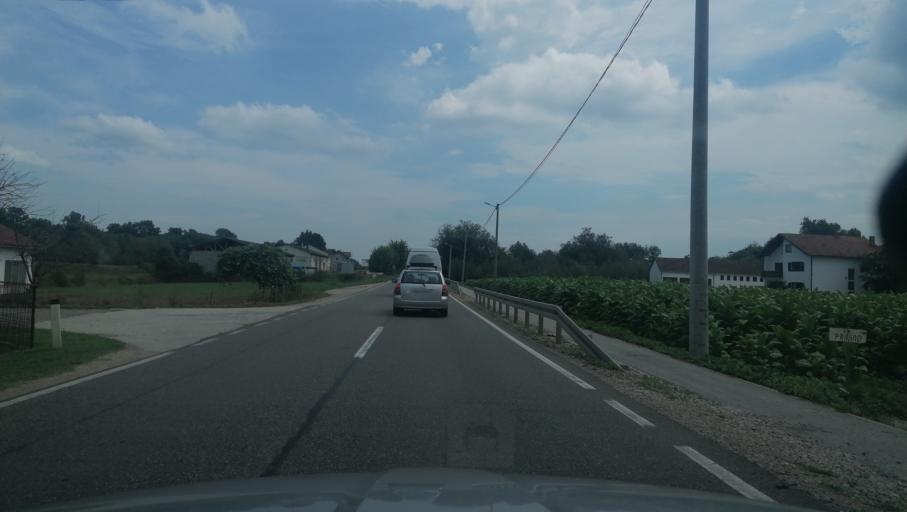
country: BA
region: Republika Srpska
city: Obudovac
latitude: 44.9595
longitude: 18.6262
